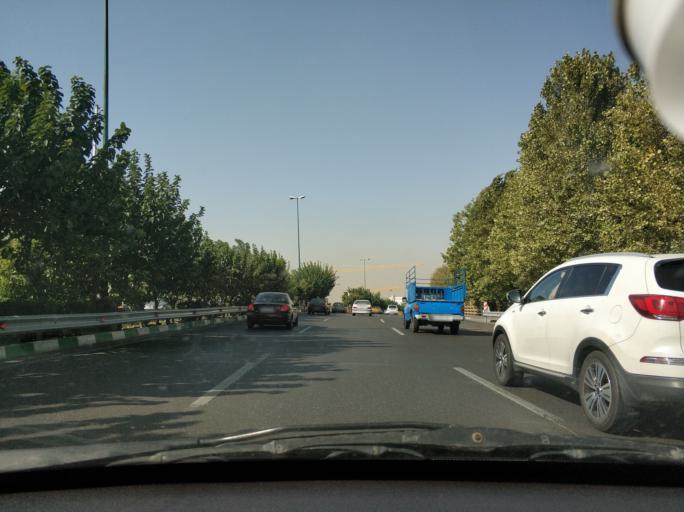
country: IR
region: Tehran
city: Tehran
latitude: 35.7416
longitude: 51.3982
